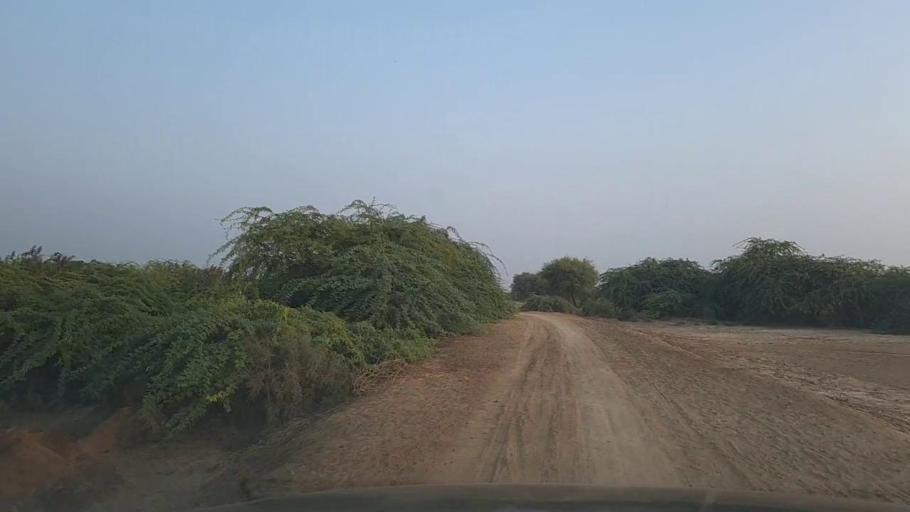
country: PK
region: Sindh
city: Jati
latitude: 24.5390
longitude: 68.4032
